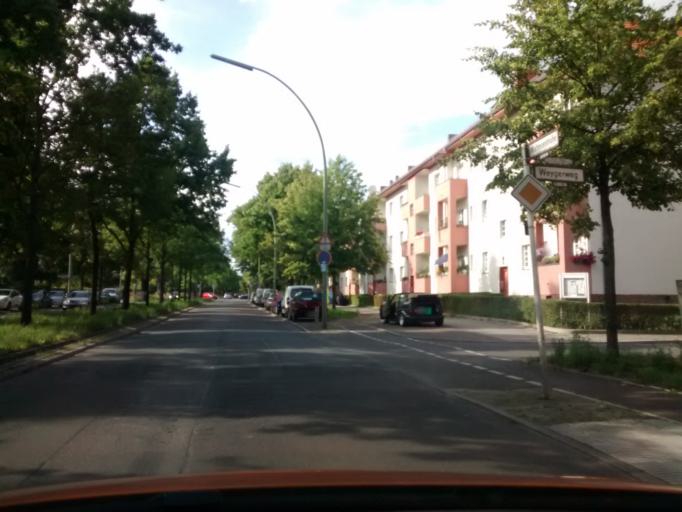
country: DE
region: Berlin
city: Marienfelde
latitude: 52.4233
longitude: 13.3574
